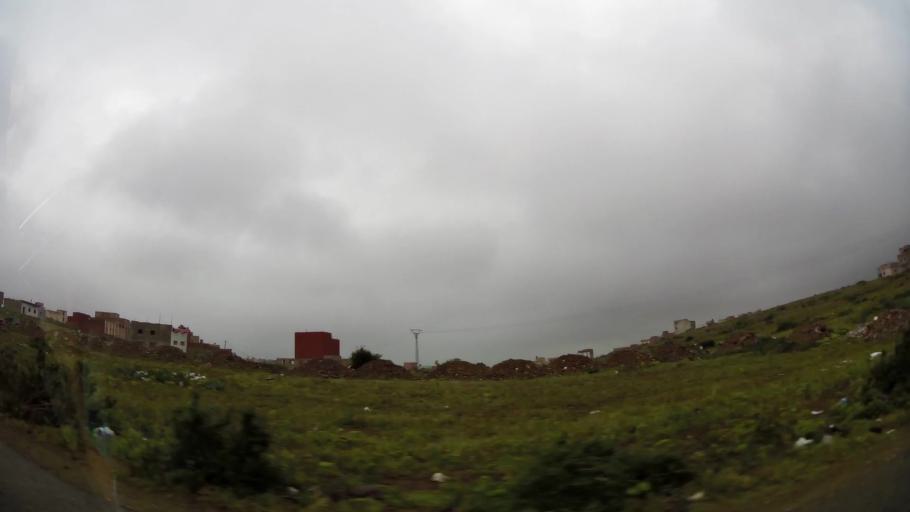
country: MA
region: Oriental
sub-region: Nador
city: Nador
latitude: 35.1847
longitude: -2.9387
